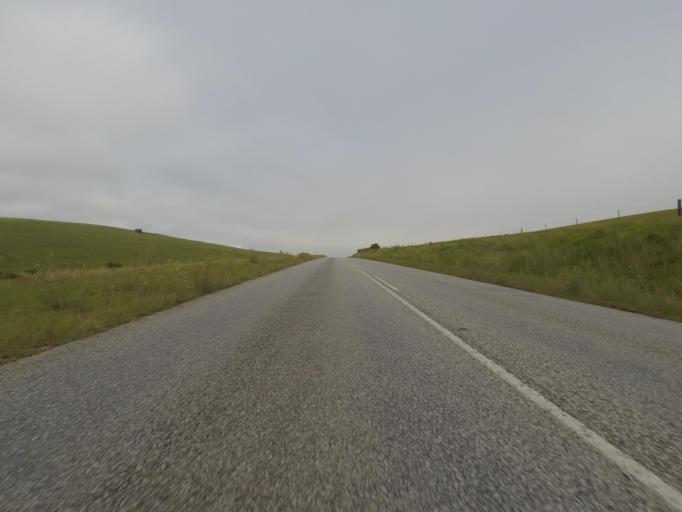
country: ZA
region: Eastern Cape
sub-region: Cacadu District Municipality
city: Port Alfred
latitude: -33.6079
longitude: 26.8185
